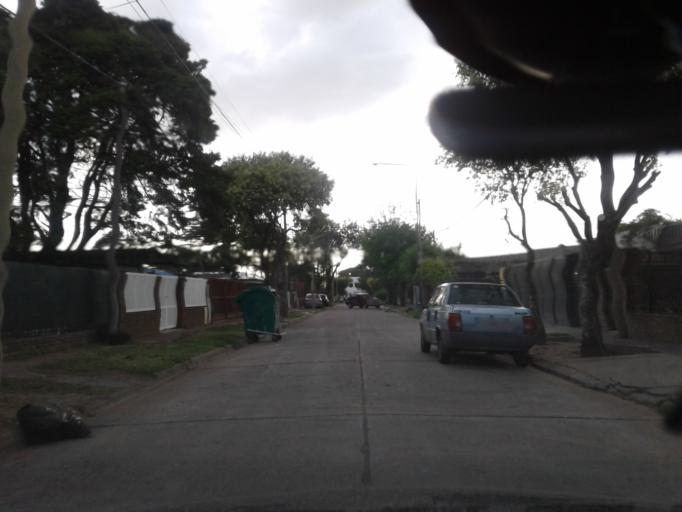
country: AR
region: Santa Fe
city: Granadero Baigorria
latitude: -32.8829
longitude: -60.7289
